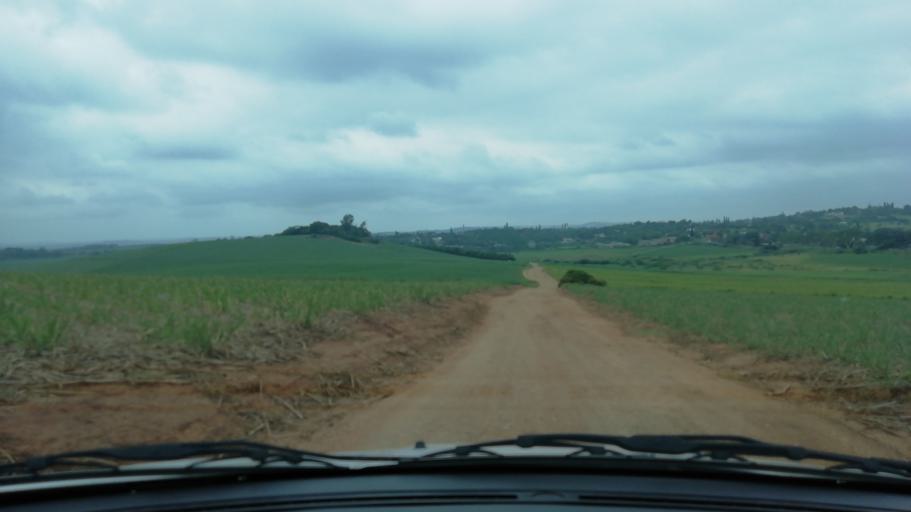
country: ZA
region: KwaZulu-Natal
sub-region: uThungulu District Municipality
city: Empangeni
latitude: -28.7315
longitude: 31.9080
